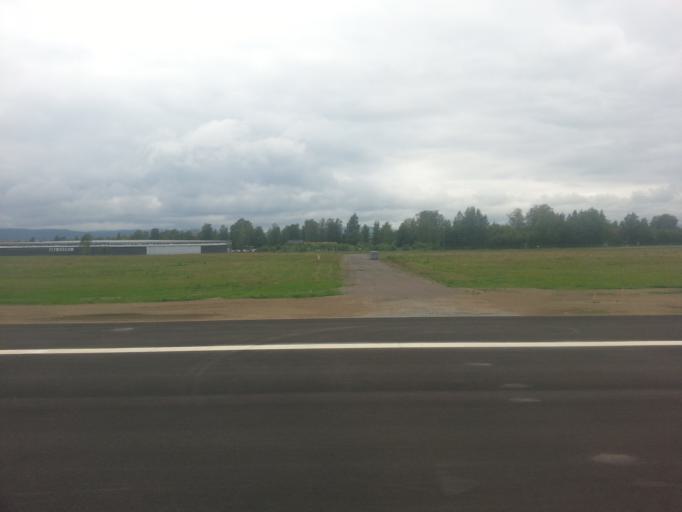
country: NO
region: Akershus
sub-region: Nannestad
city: Teigebyen
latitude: 60.1895
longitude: 11.0764
